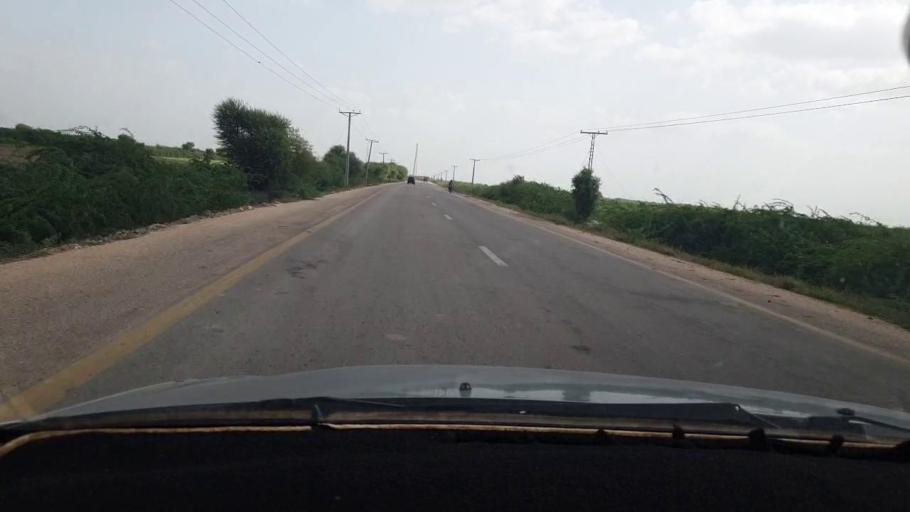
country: PK
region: Sindh
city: Naukot
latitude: 24.9210
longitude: 69.3211
